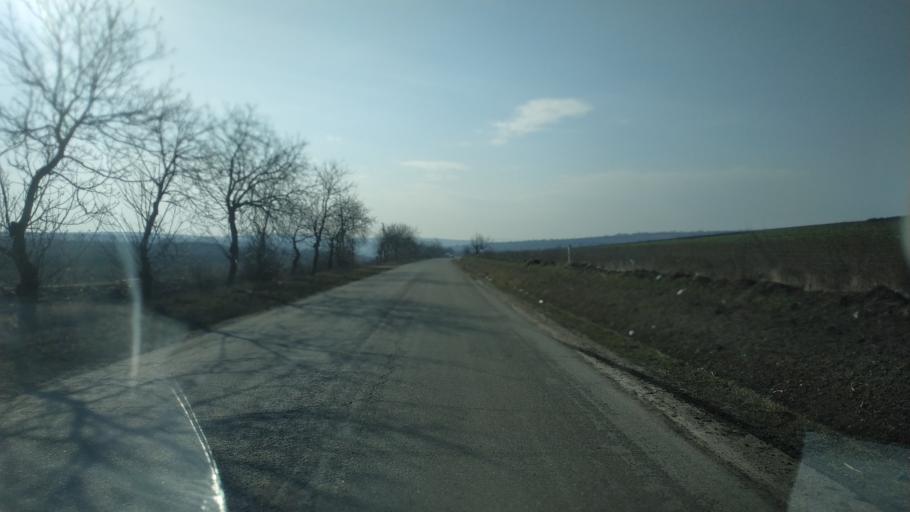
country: MD
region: Chisinau
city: Singera
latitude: 46.8501
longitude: 29.0233
